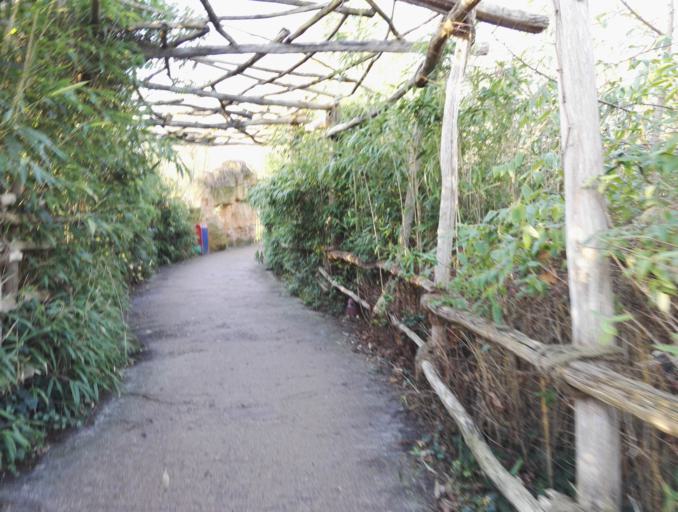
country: DE
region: Lower Saxony
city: Hannover
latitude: 52.3810
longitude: 9.7686
